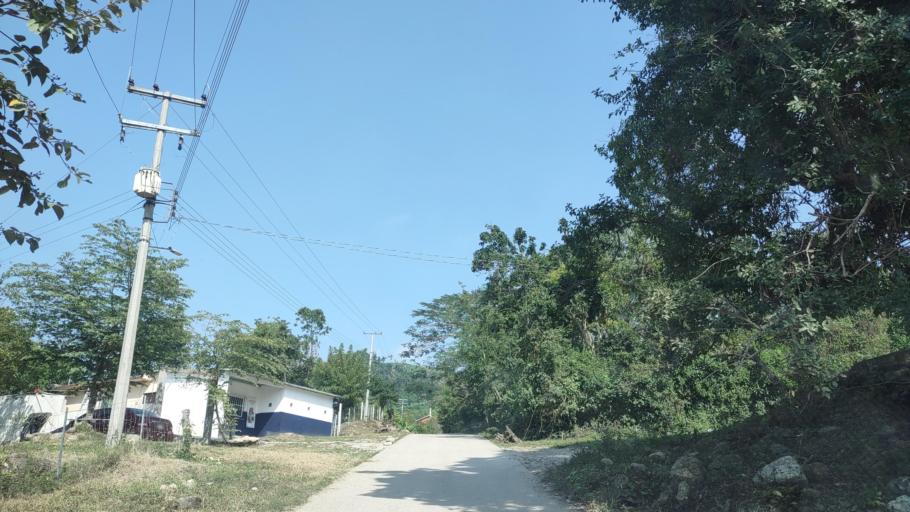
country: MX
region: Veracruz
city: Agua Dulce
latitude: 20.2946
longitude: -97.2836
